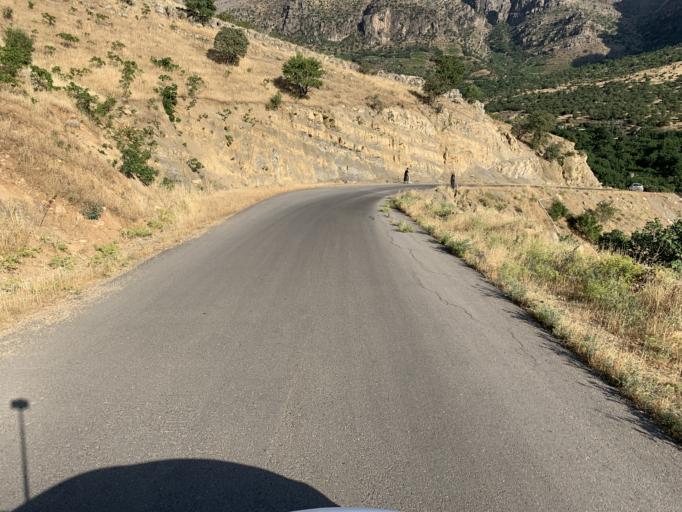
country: IQ
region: As Sulaymaniyah
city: Qeladize
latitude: 35.9940
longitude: 45.1948
